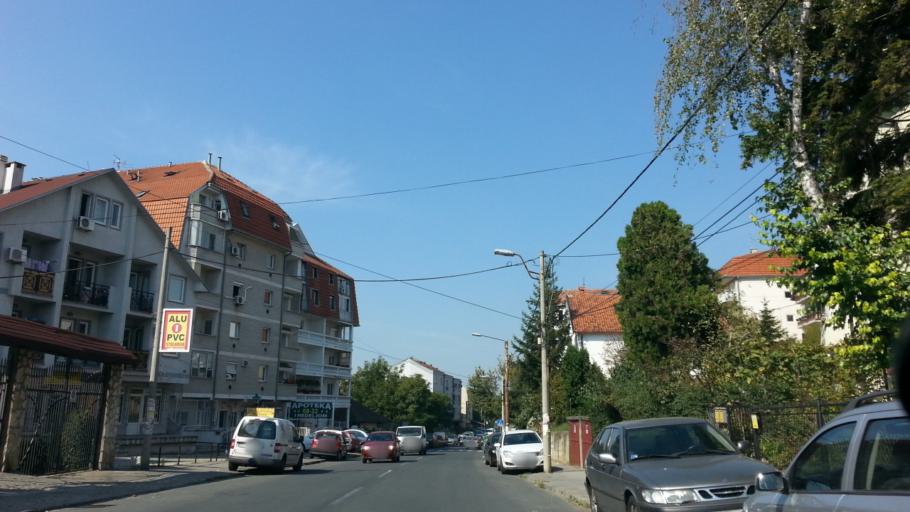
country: RS
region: Central Serbia
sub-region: Belgrade
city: Rakovica
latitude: 44.7546
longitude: 20.4229
